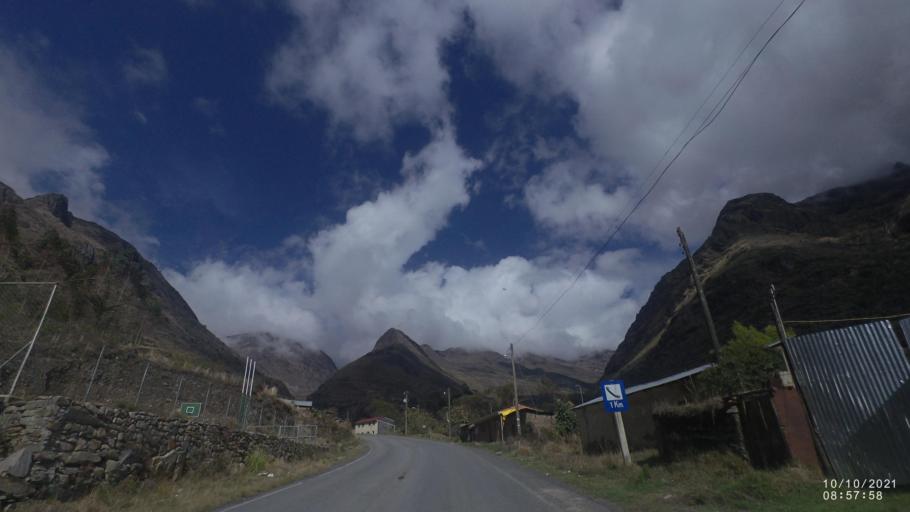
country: BO
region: La Paz
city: Quime
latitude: -16.9974
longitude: -67.2535
